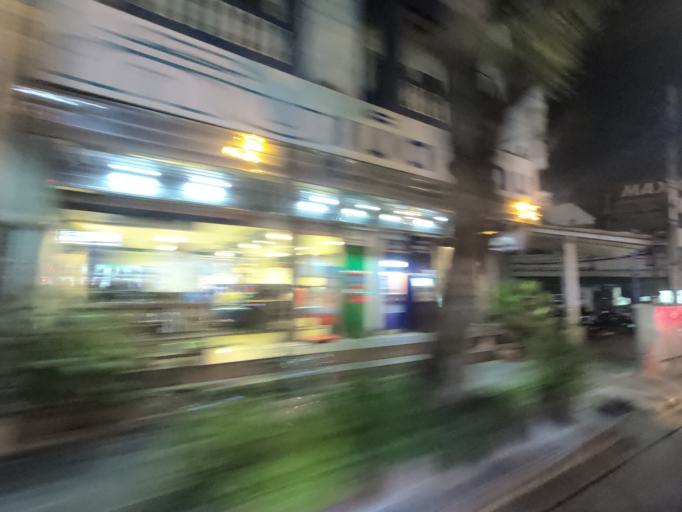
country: TH
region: Bangkok
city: Lat Phrao
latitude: 13.8086
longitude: 100.6087
